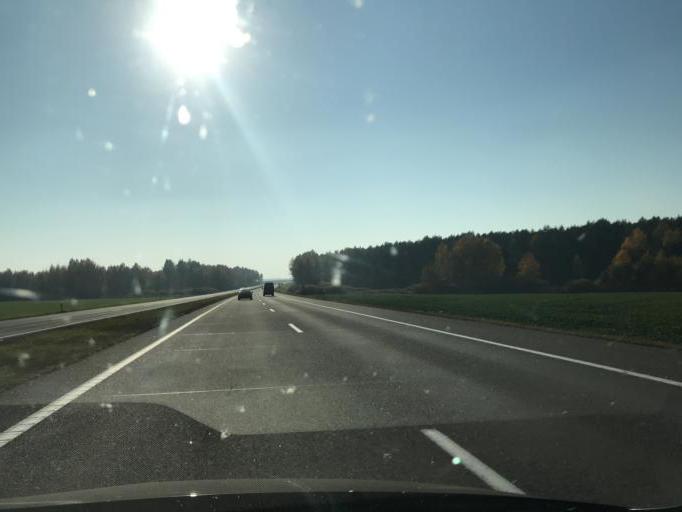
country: BY
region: Minsk
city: Haradzyeya
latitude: 53.4196
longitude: 26.5753
